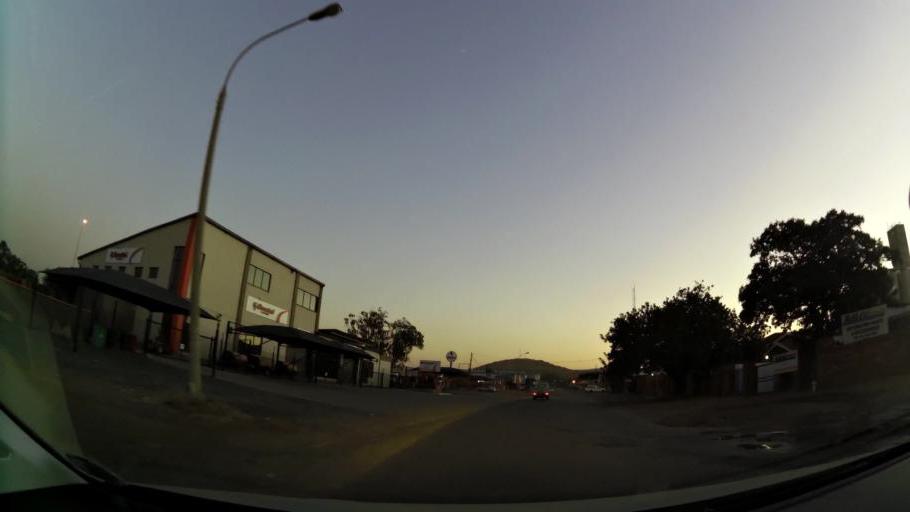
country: ZA
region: North-West
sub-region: Bojanala Platinum District Municipality
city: Rustenburg
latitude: -25.6766
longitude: 27.2590
